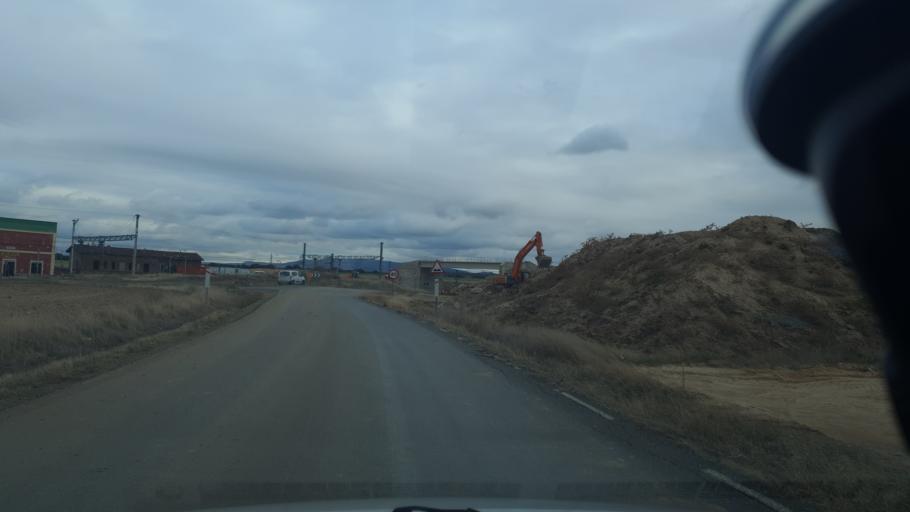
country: ES
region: Castille and Leon
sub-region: Provincia de Avila
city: Velayos
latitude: 40.8299
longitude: -4.6052
